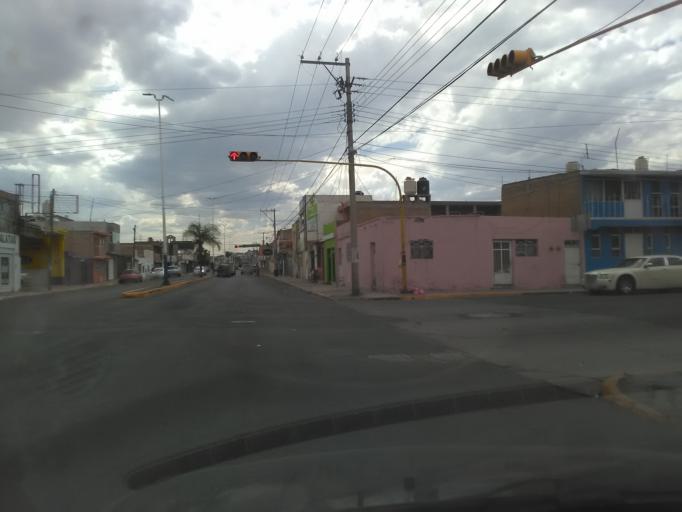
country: MX
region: Durango
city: Victoria de Durango
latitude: 24.0199
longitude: -104.6552
